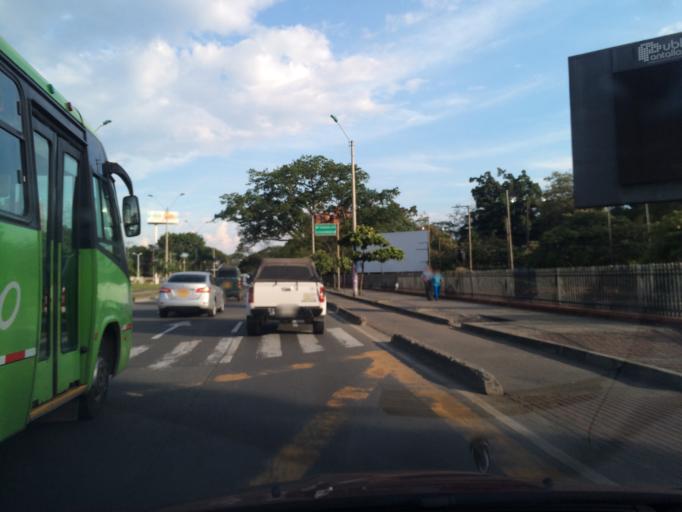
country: CO
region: Valle del Cauca
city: Cali
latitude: 3.4115
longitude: -76.5479
